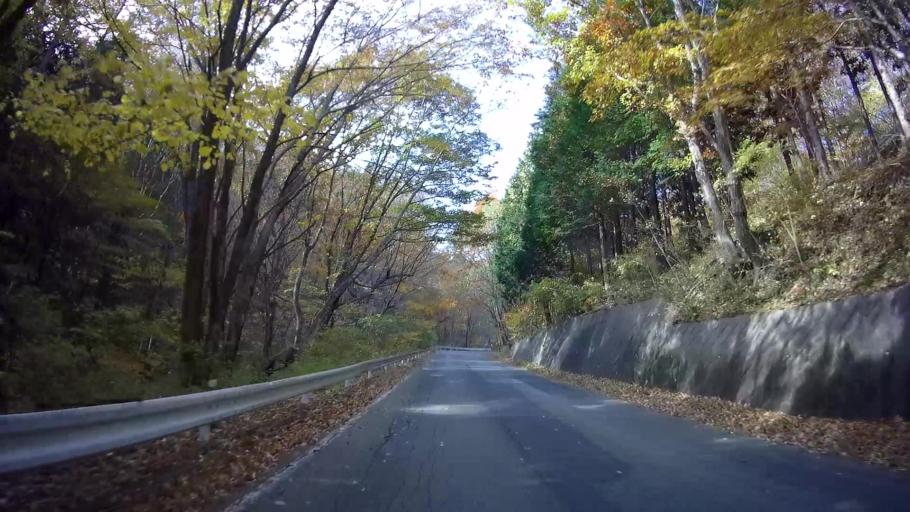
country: JP
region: Gunma
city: Nakanojomachi
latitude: 36.5157
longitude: 138.6688
